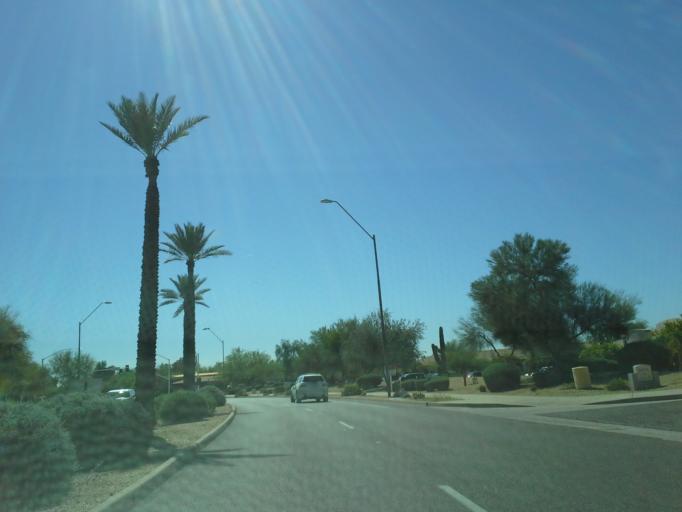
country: US
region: Arizona
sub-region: Maricopa County
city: Paradise Valley
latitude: 33.6142
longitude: -111.8978
